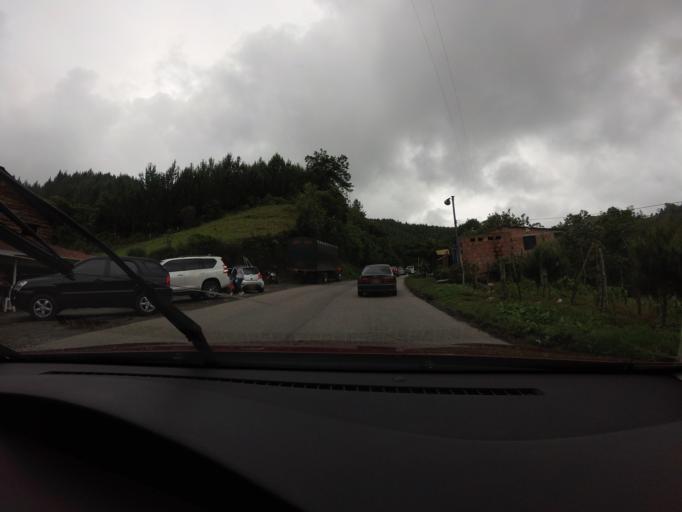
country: CO
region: Tolima
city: Herveo
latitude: 5.1359
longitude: -75.1877
